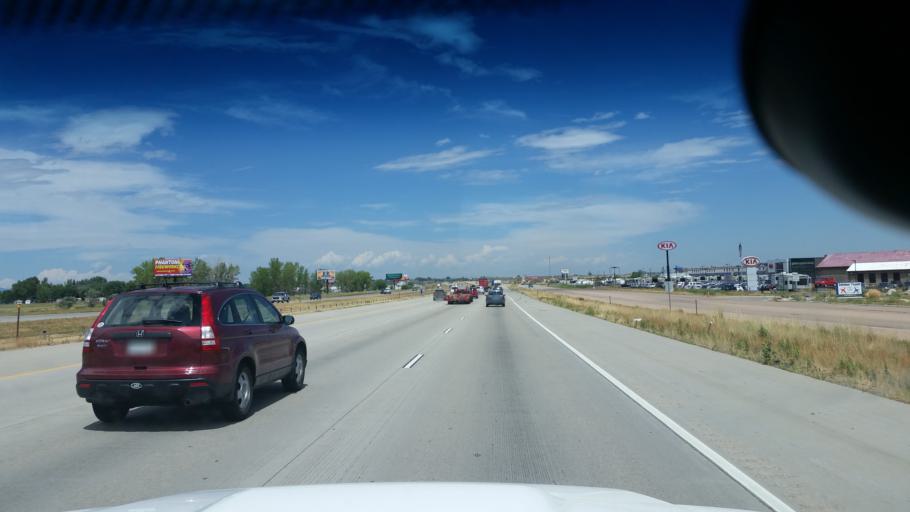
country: US
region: Colorado
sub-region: Weld County
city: Firestone
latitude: 40.1475
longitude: -104.9798
